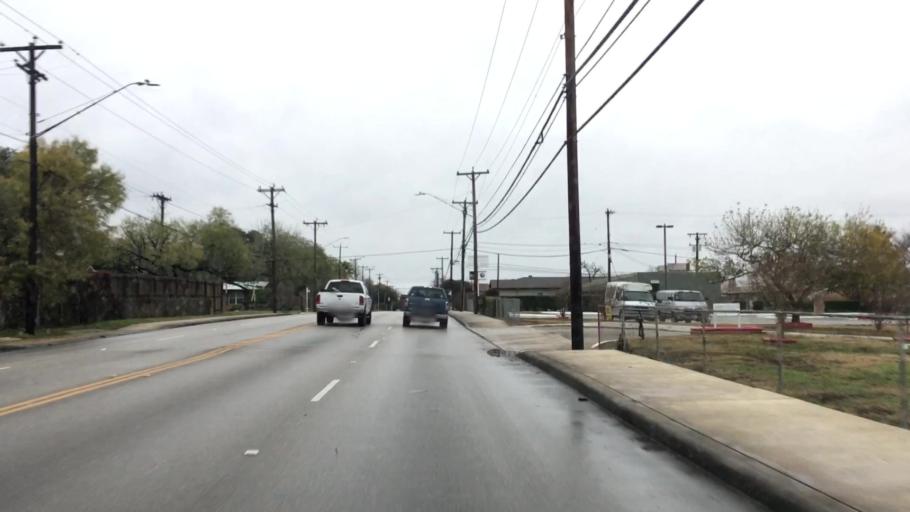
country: US
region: Texas
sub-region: Bexar County
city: Castle Hills
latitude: 29.5095
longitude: -98.5068
